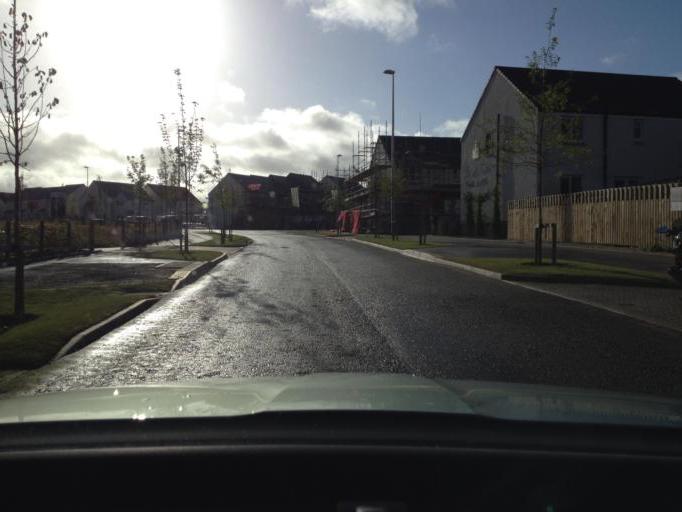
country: GB
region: Scotland
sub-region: West Lothian
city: East Calder
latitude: 55.9008
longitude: -3.4559
